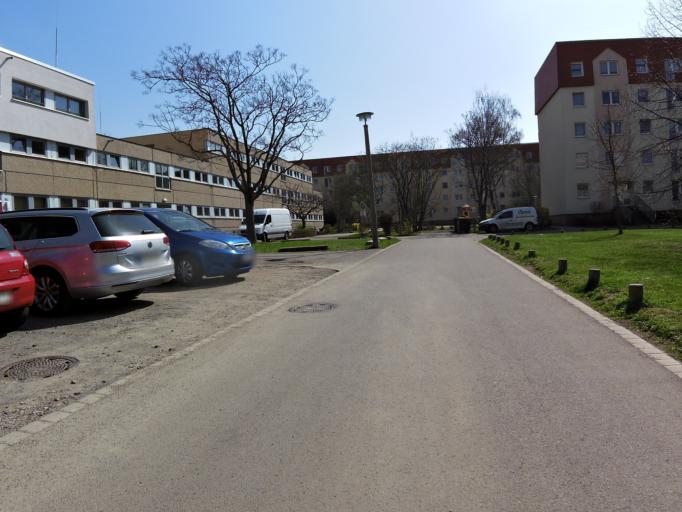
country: DE
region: Saxony
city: Leipzig
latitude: 51.3182
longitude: 12.3066
